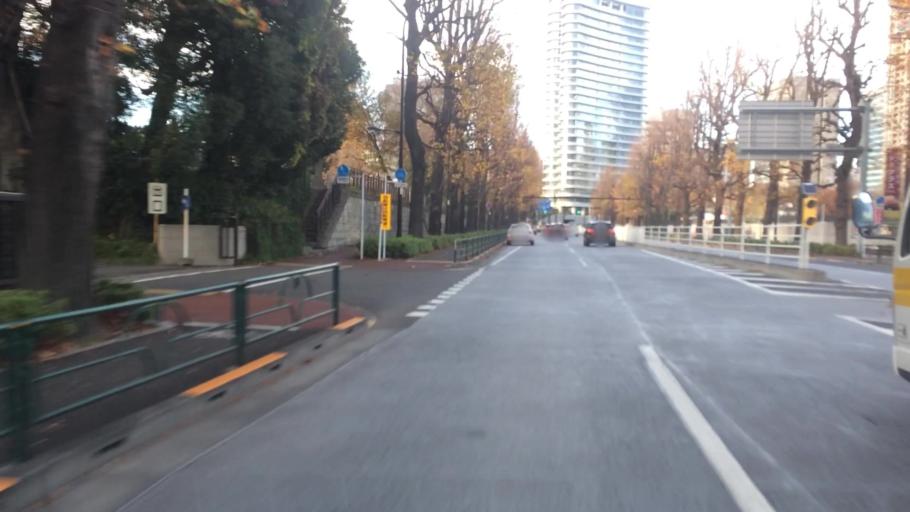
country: JP
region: Tokyo
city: Tokyo
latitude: 35.6672
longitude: 139.7242
